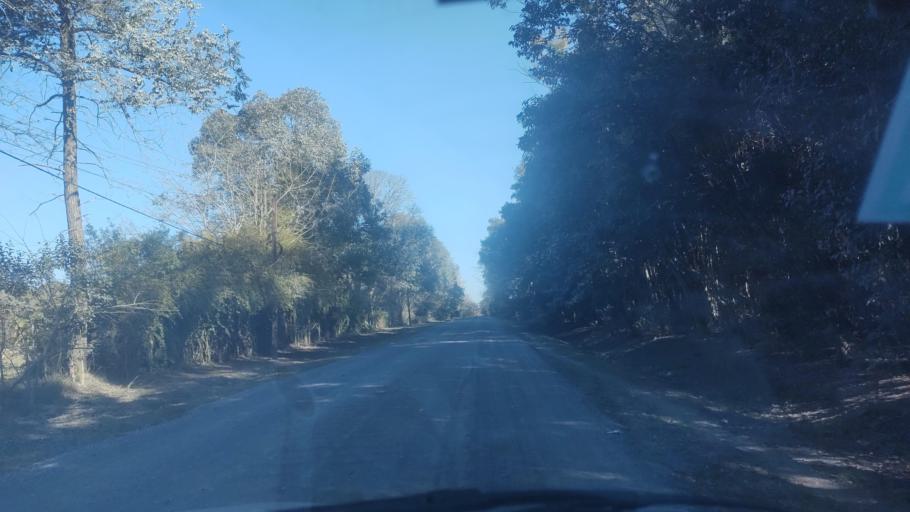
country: AR
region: Buenos Aires
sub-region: Partido de La Plata
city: La Plata
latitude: -34.8511
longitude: -58.1033
